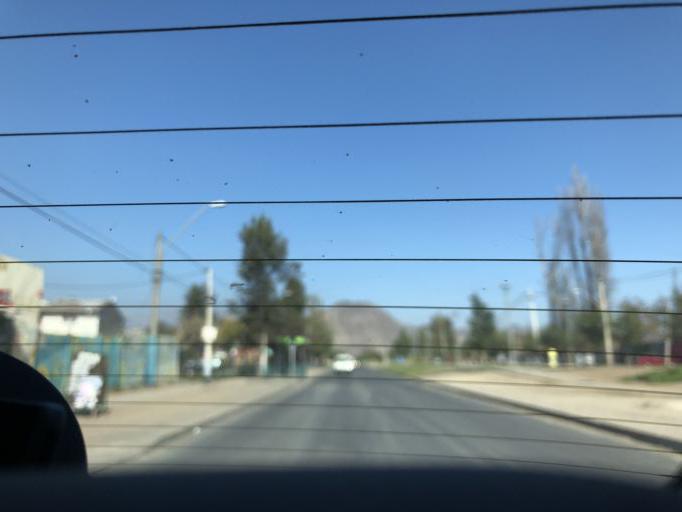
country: CL
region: Santiago Metropolitan
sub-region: Provincia de Santiago
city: La Pintana
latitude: -33.6271
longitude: -70.6284
